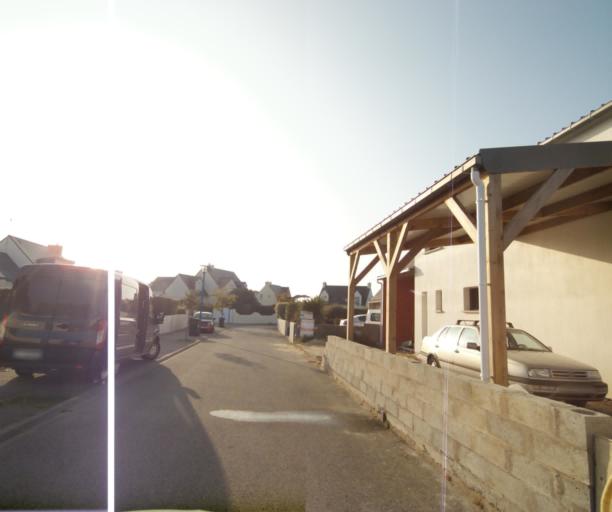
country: FR
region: Brittany
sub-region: Departement du Morbihan
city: Locmiquelic
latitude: 47.7121
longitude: -3.3388
